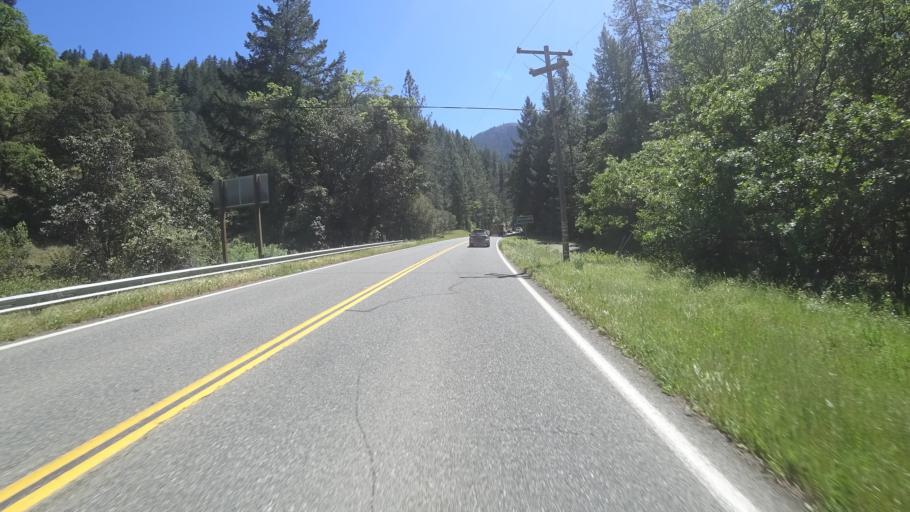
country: US
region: California
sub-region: Trinity County
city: Hayfork
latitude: 40.7803
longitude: -123.3325
